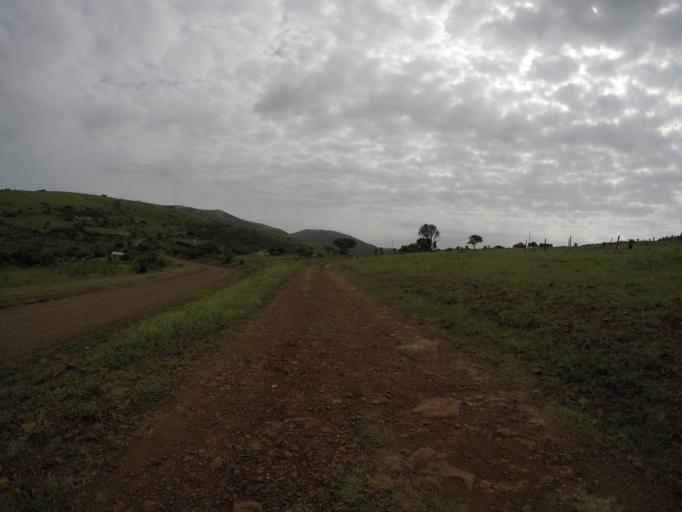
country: ZA
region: KwaZulu-Natal
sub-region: uThungulu District Municipality
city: Empangeni
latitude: -28.6307
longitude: 31.9055
